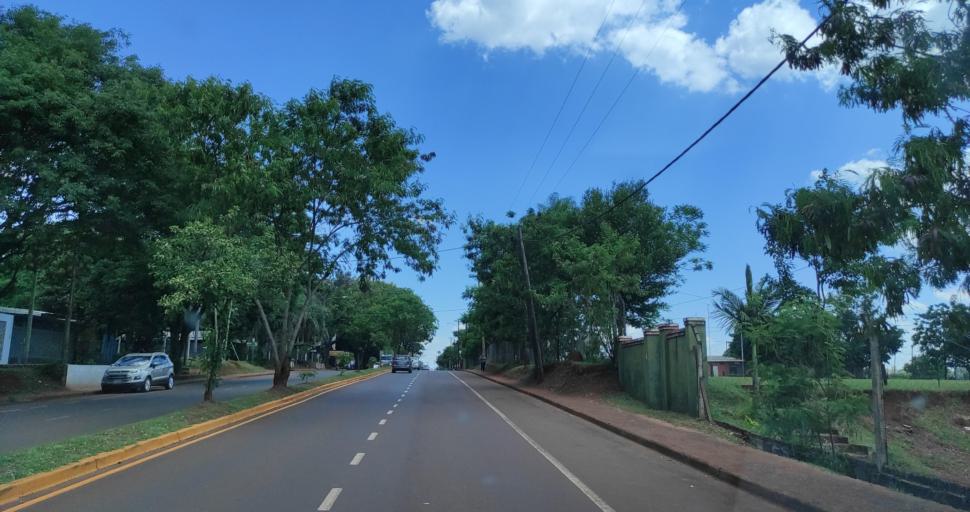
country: AR
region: Misiones
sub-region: Departamento de Capital
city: Posadas
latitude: -27.3941
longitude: -55.9431
